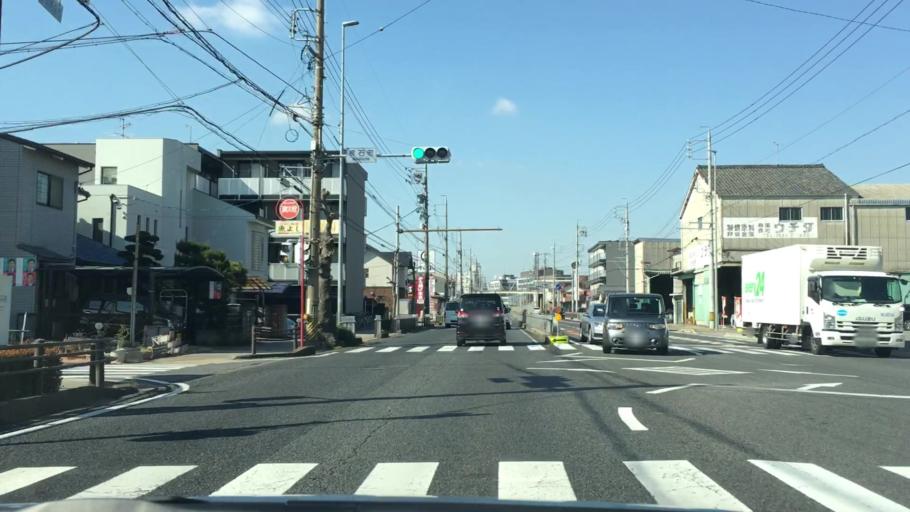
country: JP
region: Aichi
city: Okazaki
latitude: 34.9505
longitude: 137.1808
